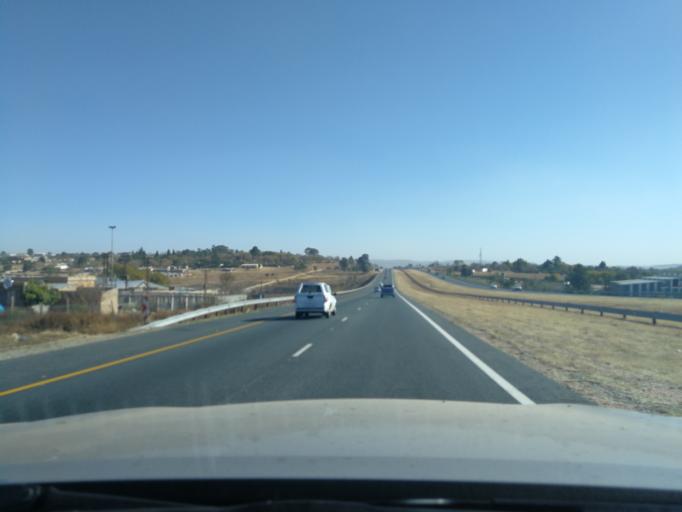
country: ZA
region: Gauteng
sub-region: West Rand District Municipality
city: Muldersdriseloop
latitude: -26.0137
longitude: 27.8774
